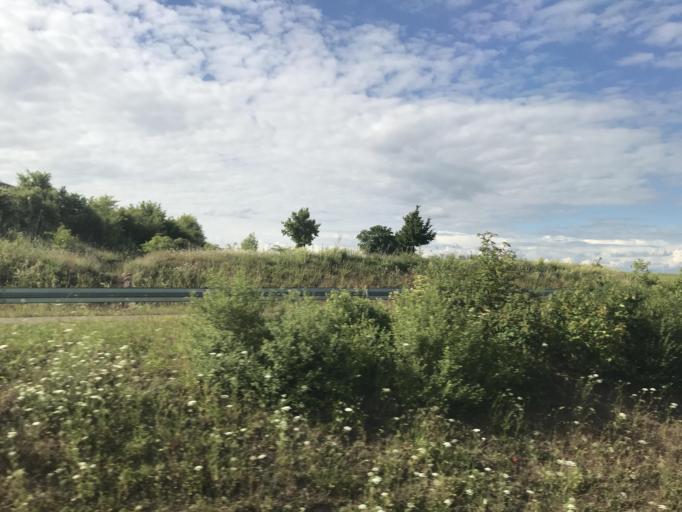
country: DE
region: Thuringia
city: Ballstedt
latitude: 51.0628
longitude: 11.2115
